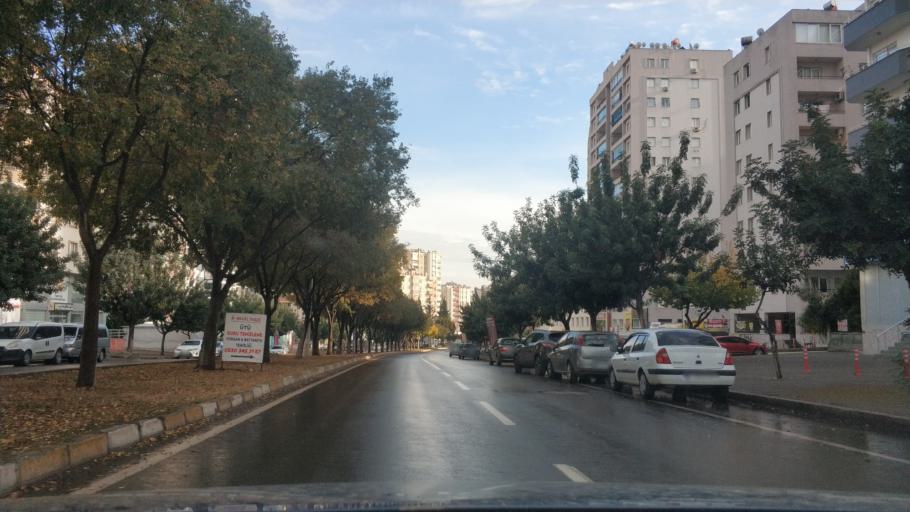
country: TR
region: Adana
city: Seyhan
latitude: 37.0393
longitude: 35.2768
